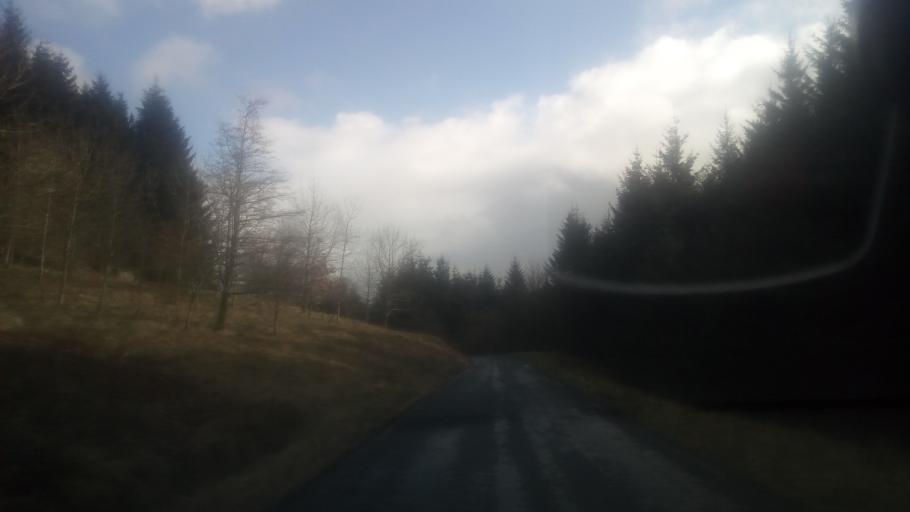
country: GB
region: Scotland
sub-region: The Scottish Borders
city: Innerleithen
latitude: 55.4675
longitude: -3.1378
